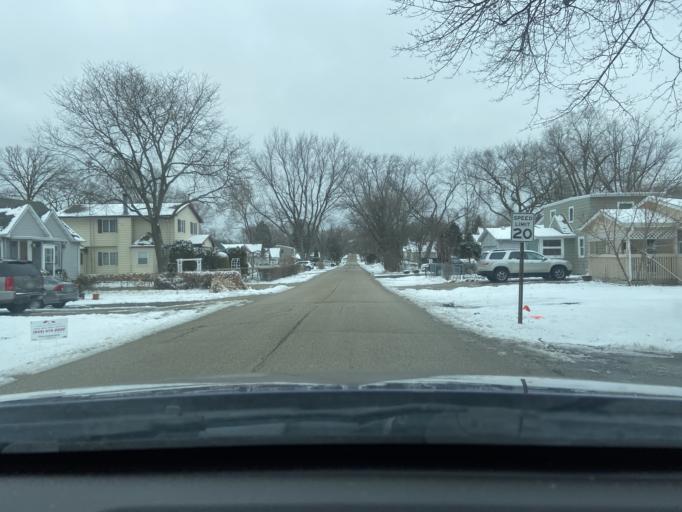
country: US
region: Illinois
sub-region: Lake County
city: Round Lake Park
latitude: 42.3519
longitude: -88.0797
